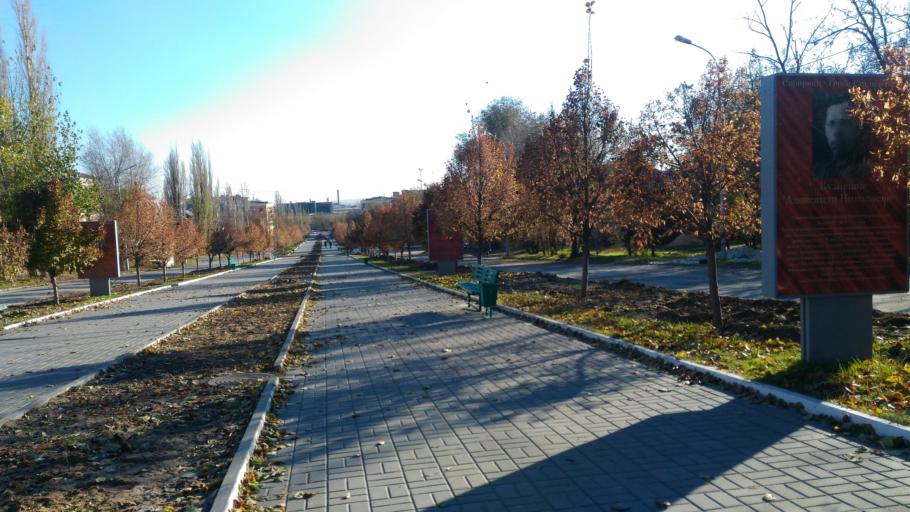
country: RU
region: Volgograd
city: Volgograd
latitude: 48.6632
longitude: 44.4436
